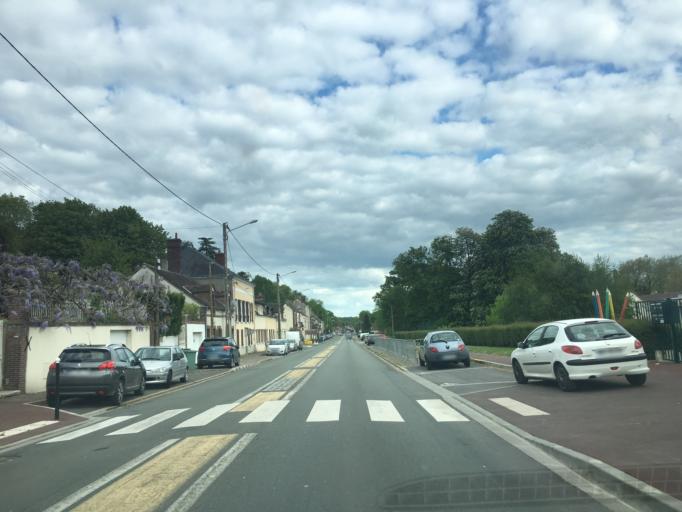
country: FR
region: Haute-Normandie
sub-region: Departement de l'Eure
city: La Madeleine-de-Nonancourt
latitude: 48.7698
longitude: 1.2018
